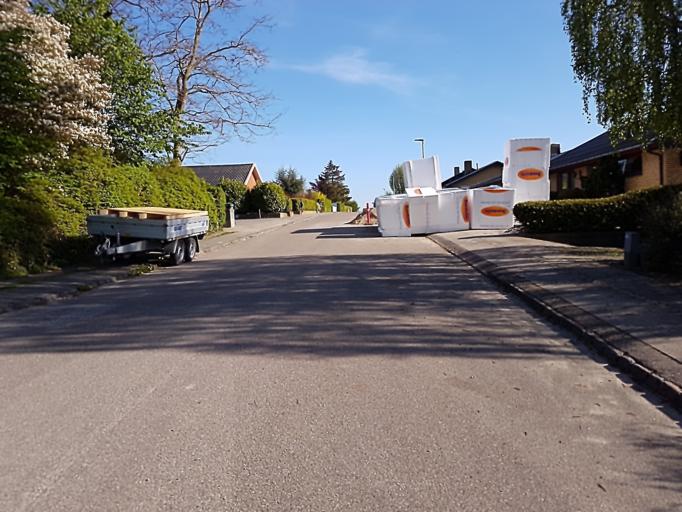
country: DK
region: Capital Region
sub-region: Egedal Kommune
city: Olstykke
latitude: 55.7923
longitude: 12.1488
